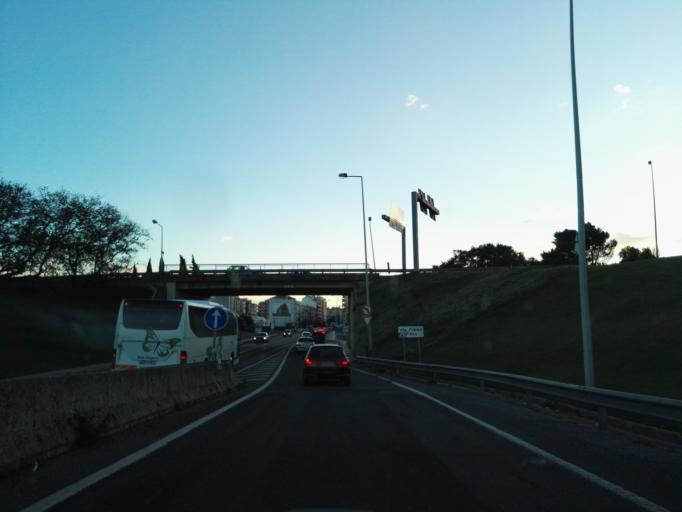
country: PT
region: Lisbon
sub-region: Vila Franca de Xira
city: Vila Franca de Xira
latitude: 38.9612
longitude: -8.9855
